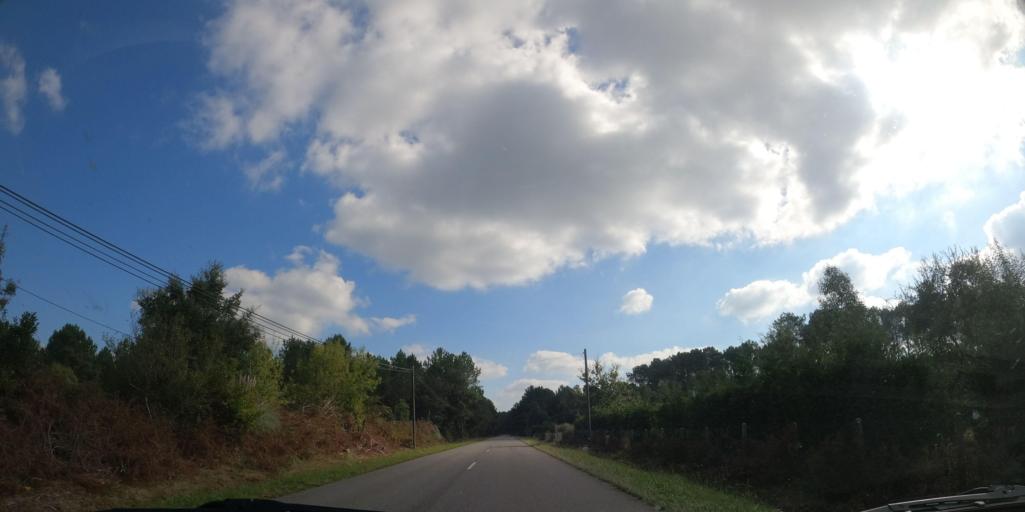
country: FR
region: Aquitaine
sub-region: Departement des Landes
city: Soustons
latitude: 43.7404
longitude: -1.2978
